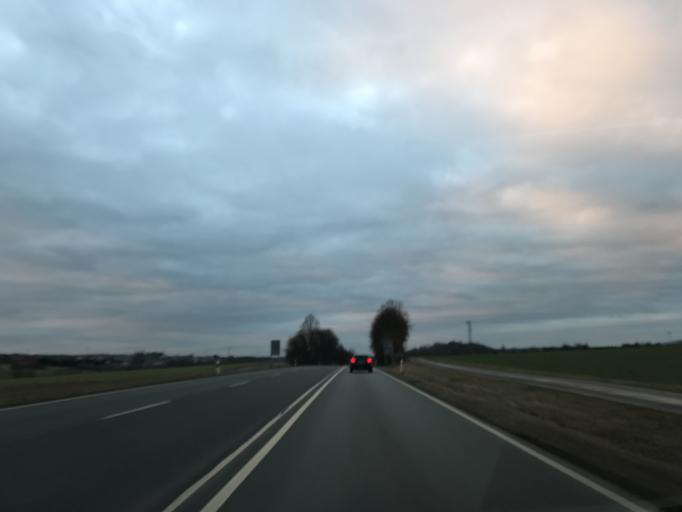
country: DE
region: Hesse
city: Grebenstein
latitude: 51.4612
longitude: 9.4060
